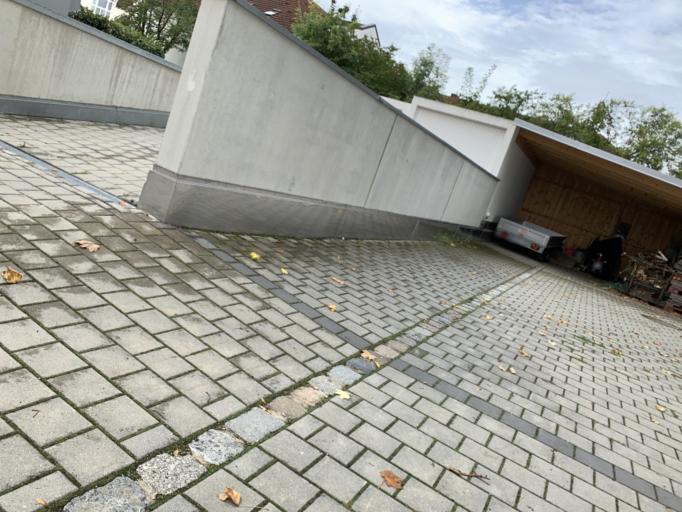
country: DE
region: Bavaria
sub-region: Upper Bavaria
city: Freising
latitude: 48.3915
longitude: 11.7616
